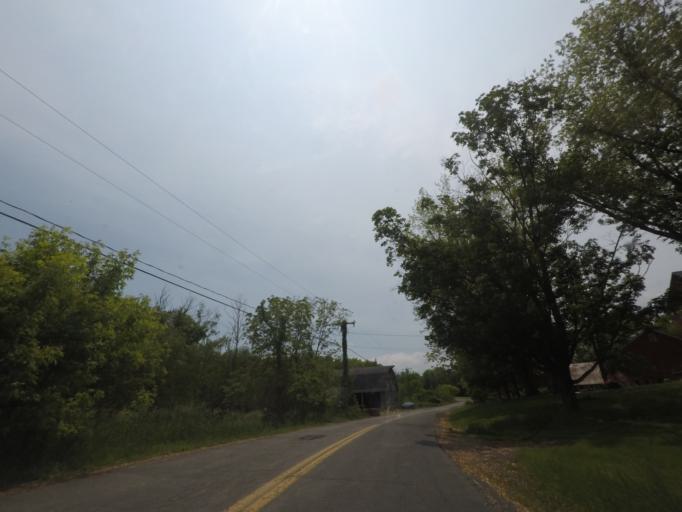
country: US
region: New York
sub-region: Rensselaer County
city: Castleton-on-Hudson
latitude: 42.5008
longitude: -73.7054
